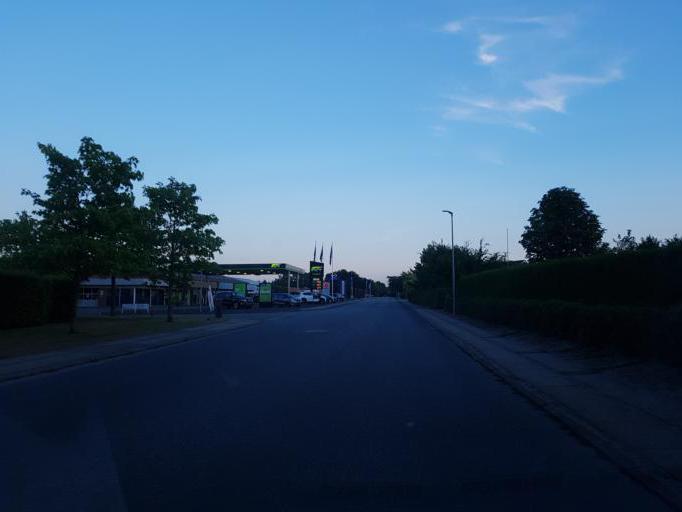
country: DK
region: South Denmark
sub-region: Vejen Kommune
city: Vejen
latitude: 55.4665
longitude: 9.1342
